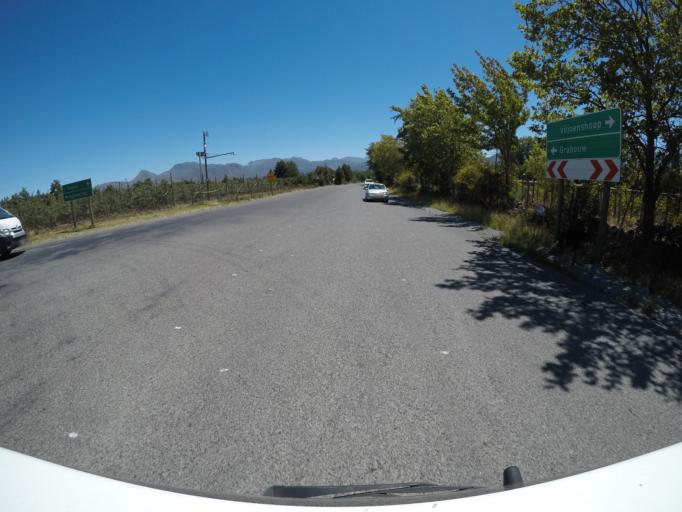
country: ZA
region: Western Cape
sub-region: Overberg District Municipality
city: Grabouw
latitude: -34.1750
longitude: 19.0342
